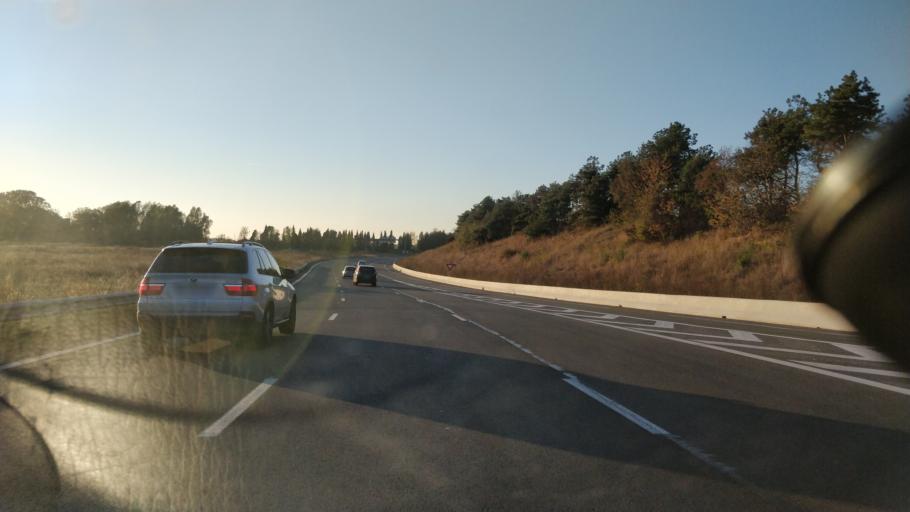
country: FR
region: Ile-de-France
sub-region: Departement de Seine-et-Marne
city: Bailly-Romainvilliers
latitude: 48.8422
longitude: 2.8200
